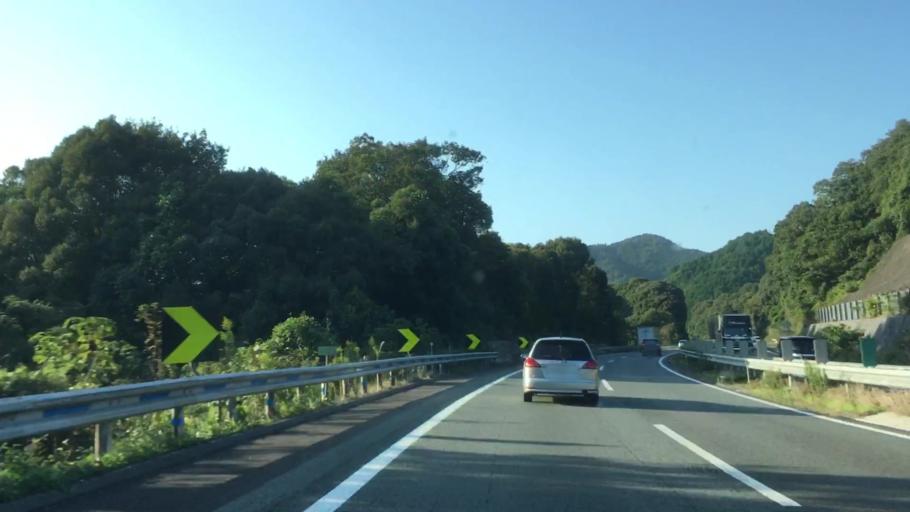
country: JP
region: Yamaguchi
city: Ogori-shimogo
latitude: 34.1307
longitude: 131.3772
